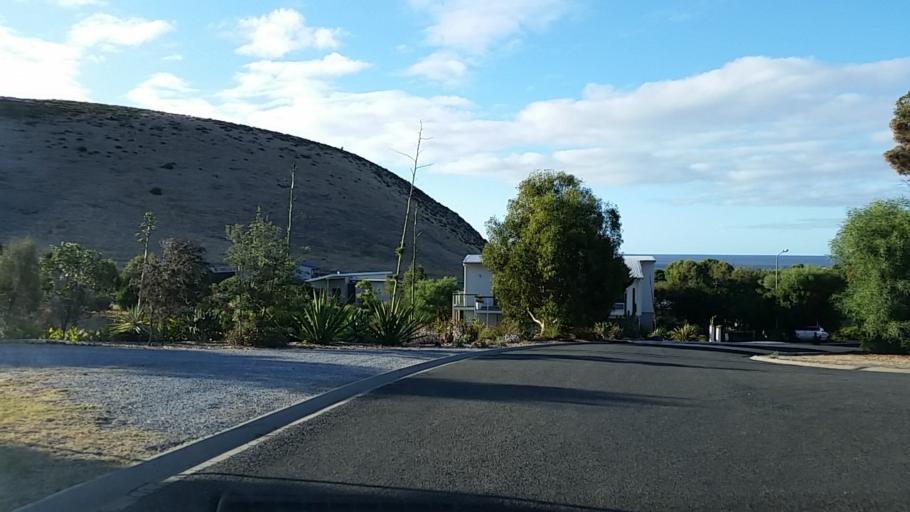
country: AU
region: South Australia
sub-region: Yankalilla
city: Normanville
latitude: -35.5156
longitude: 138.2166
